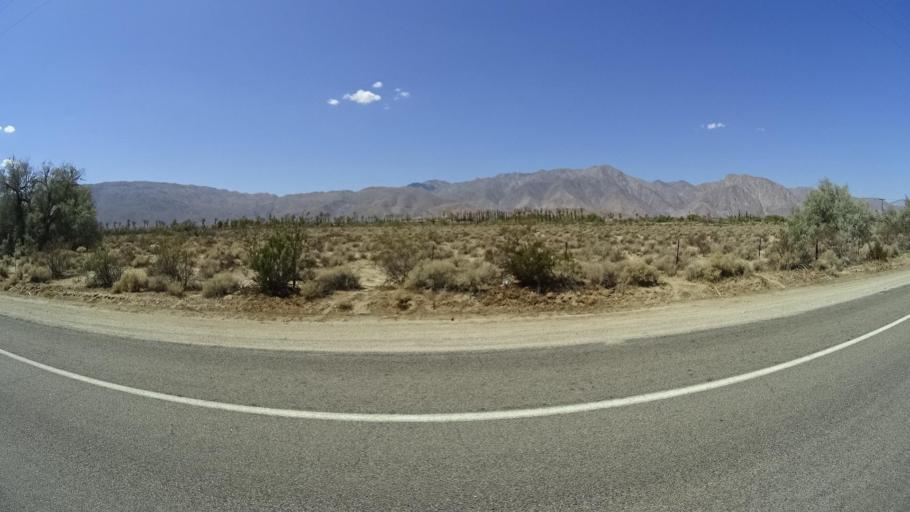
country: US
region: California
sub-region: San Diego County
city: Borrego Springs
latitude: 33.2370
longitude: -116.3480
